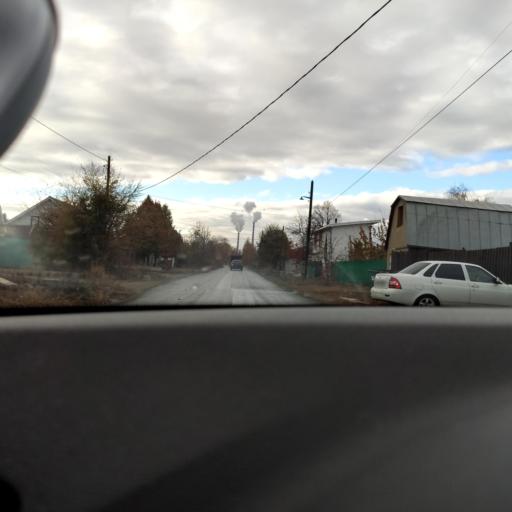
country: RU
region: Samara
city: Petra-Dubrava
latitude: 53.2485
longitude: 50.3247
